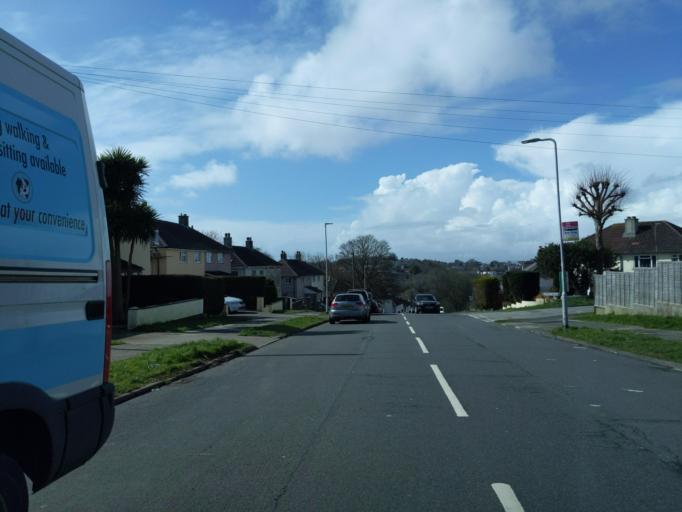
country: GB
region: England
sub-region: Plymouth
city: Plymouth
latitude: 50.3888
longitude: -4.1122
